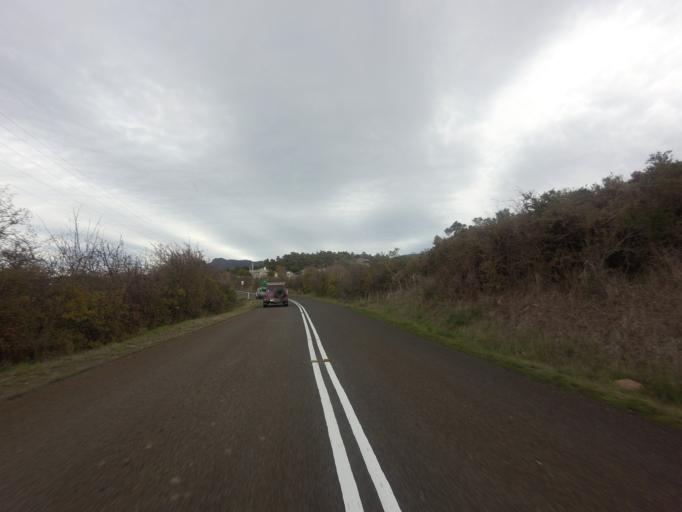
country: AU
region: Tasmania
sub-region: Brighton
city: Bridgewater
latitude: -42.6519
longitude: 147.1251
